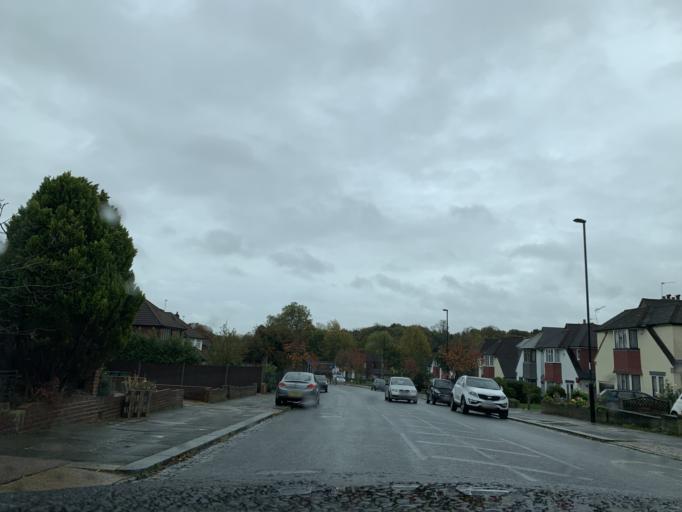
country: GB
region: England
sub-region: Greater London
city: Blackheath
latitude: 51.4417
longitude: 0.0267
